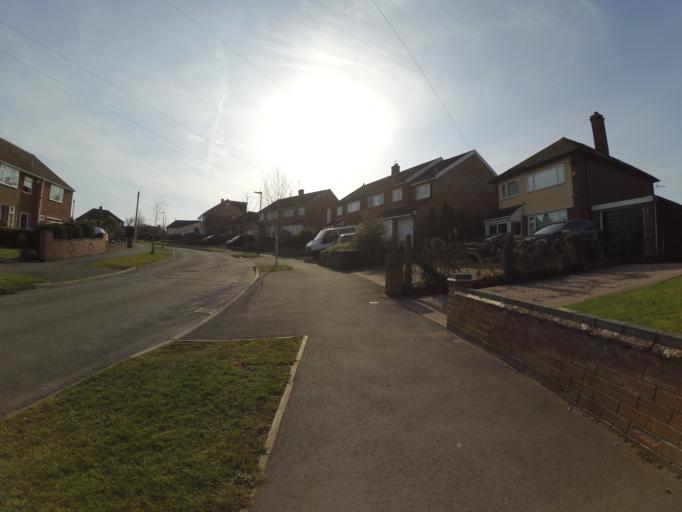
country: GB
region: England
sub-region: Warwickshire
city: Rugby
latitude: 52.3673
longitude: -1.2332
